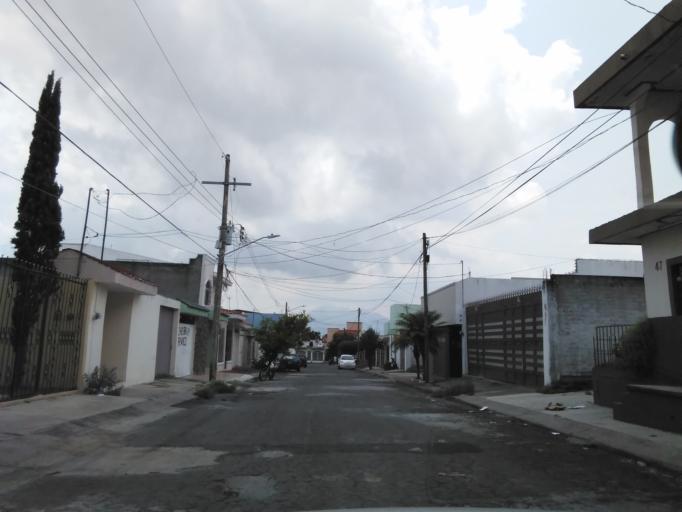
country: MX
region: Nayarit
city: Tepic
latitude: 21.5174
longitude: -104.9195
